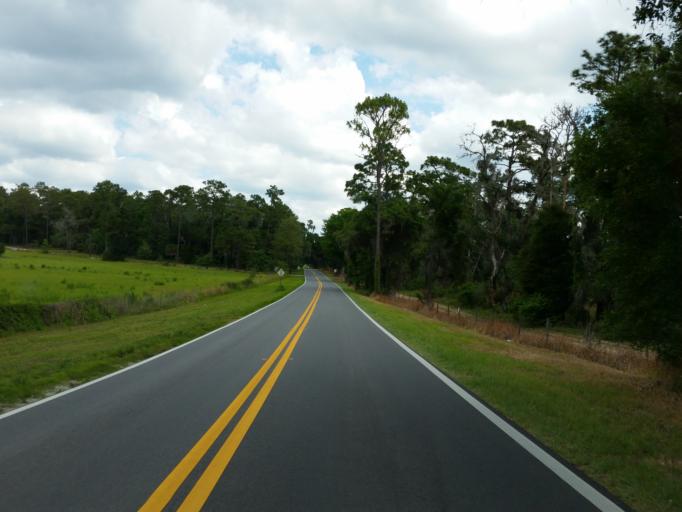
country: US
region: Florida
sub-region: Hernando County
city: North Brooksville
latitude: 28.6130
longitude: -82.3593
